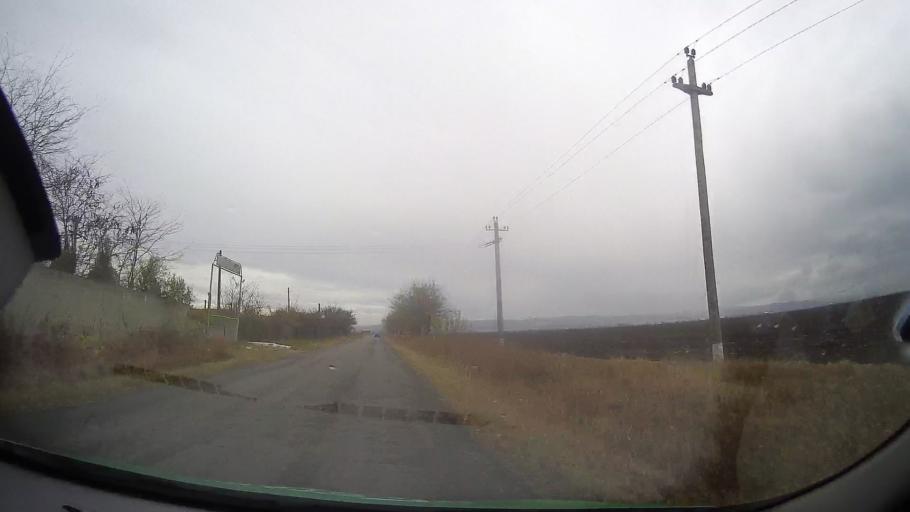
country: RO
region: Prahova
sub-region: Comuna Colceag
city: Inotesti
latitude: 44.9731
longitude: 26.3424
